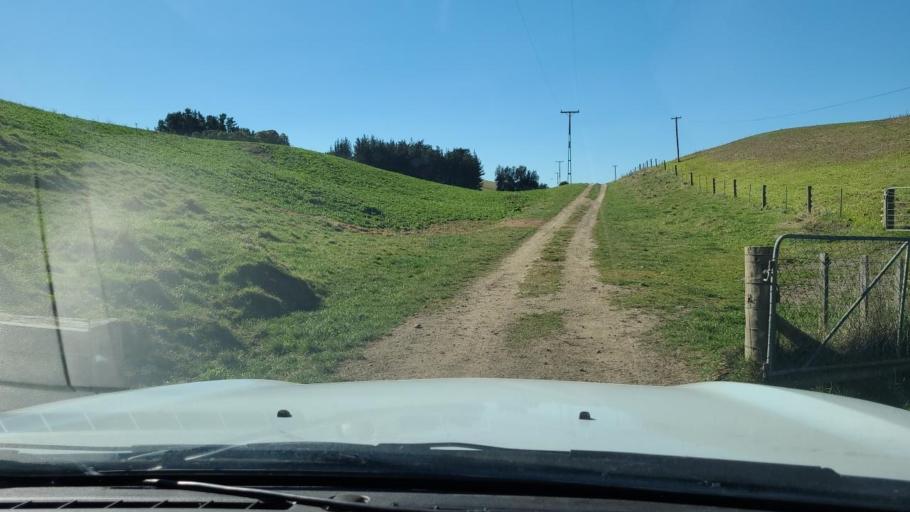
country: NZ
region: Hawke's Bay
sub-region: Hastings District
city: Hastings
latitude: -39.7942
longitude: 176.6517
